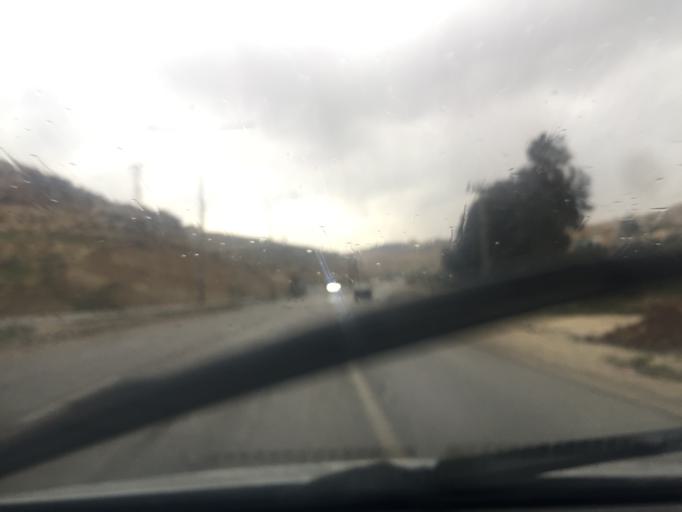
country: JO
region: Zarqa
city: Russeifa
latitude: 32.0177
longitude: 35.9906
